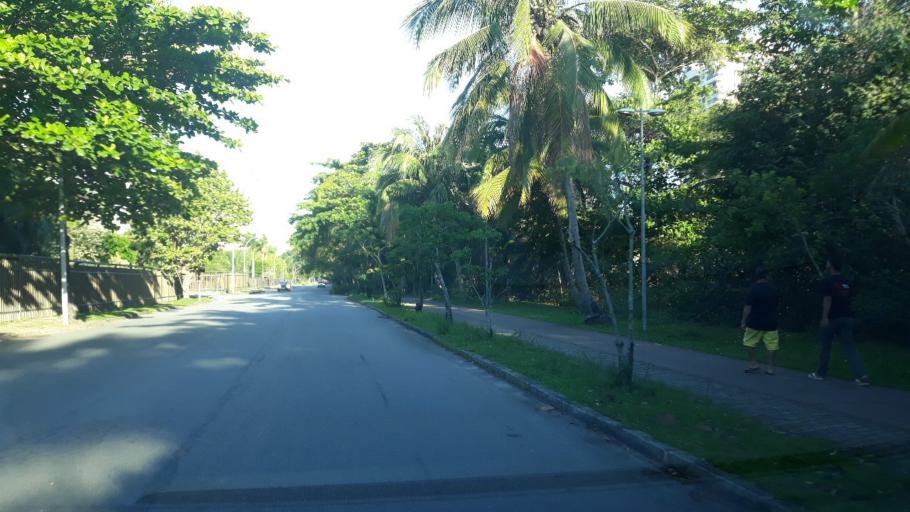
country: BR
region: Rio de Janeiro
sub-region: Rio De Janeiro
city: Rio de Janeiro
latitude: -23.0058
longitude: -43.3452
